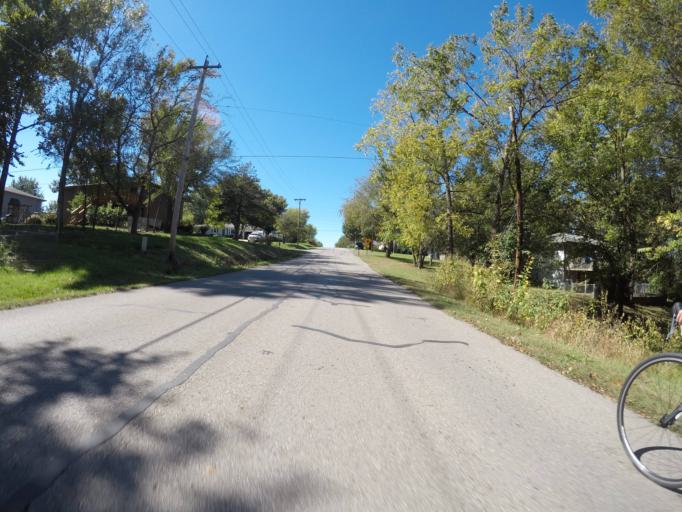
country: US
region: Kansas
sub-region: Douglas County
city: Eudora
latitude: 38.9389
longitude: -95.0993
